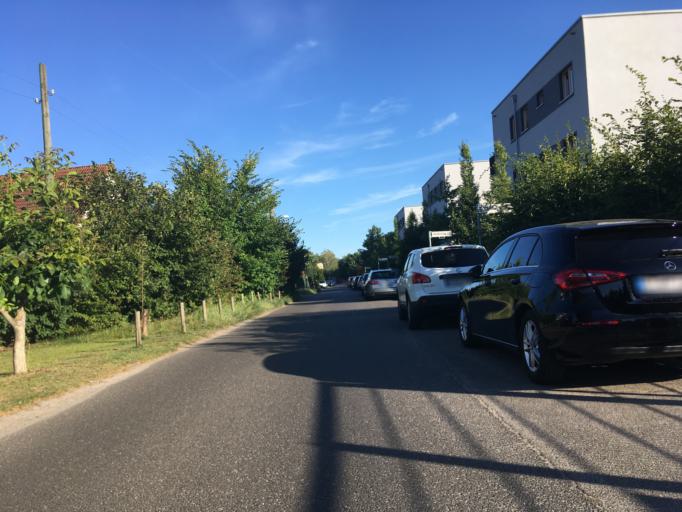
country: DE
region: Berlin
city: Grunau
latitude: 52.4257
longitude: 13.5694
